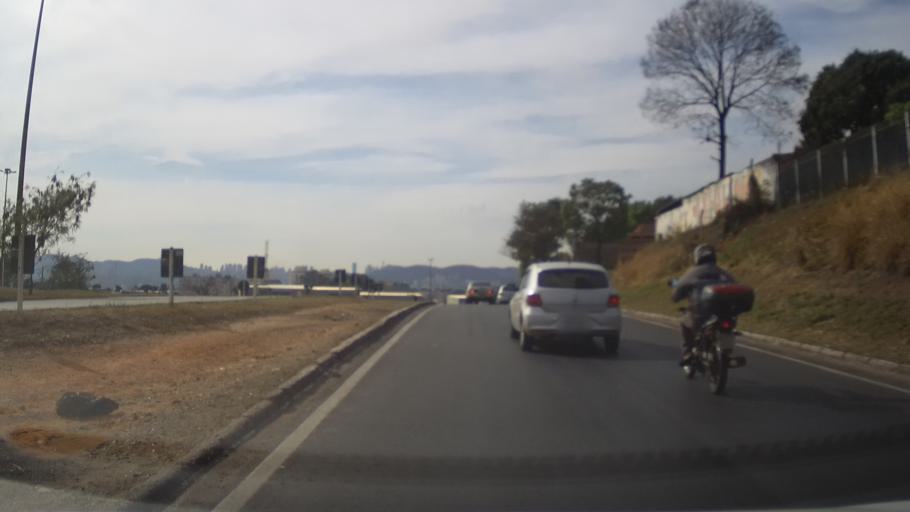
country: BR
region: Minas Gerais
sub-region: Contagem
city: Contagem
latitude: -19.9266
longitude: -44.0077
